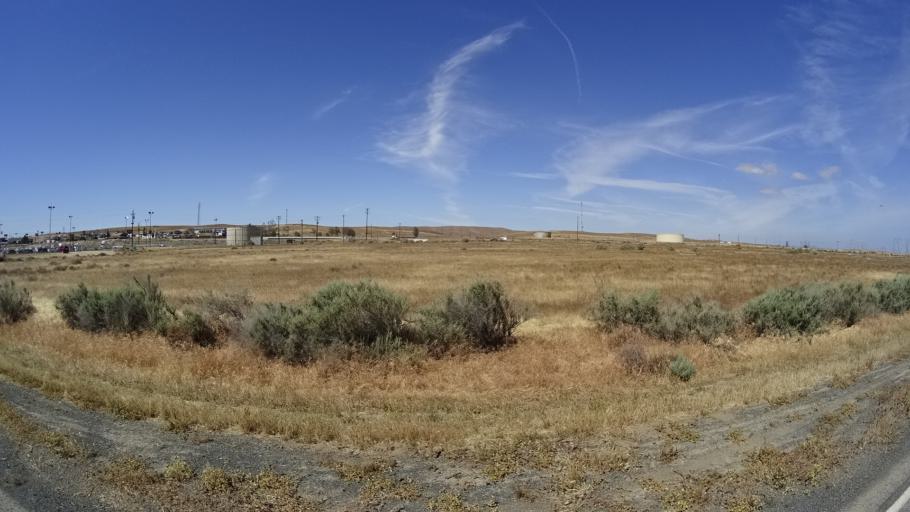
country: US
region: California
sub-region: Kings County
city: Kettleman City
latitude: 35.9938
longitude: -119.9563
